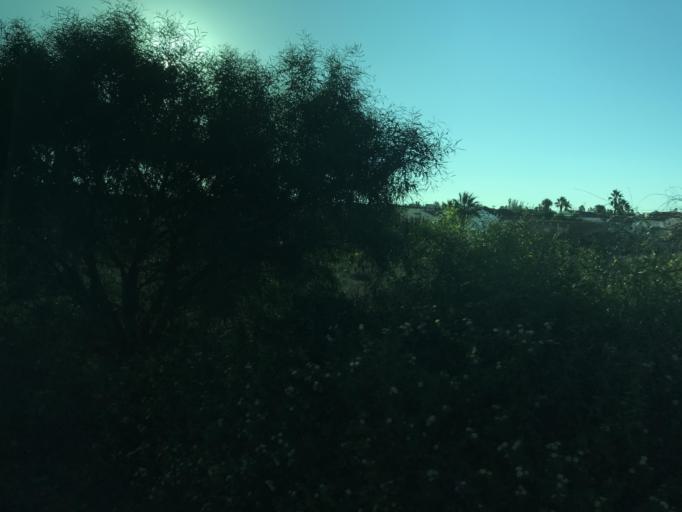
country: ES
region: Valencia
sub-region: Provincia de Alicante
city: Torrevieja
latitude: 37.9971
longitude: -0.6541
